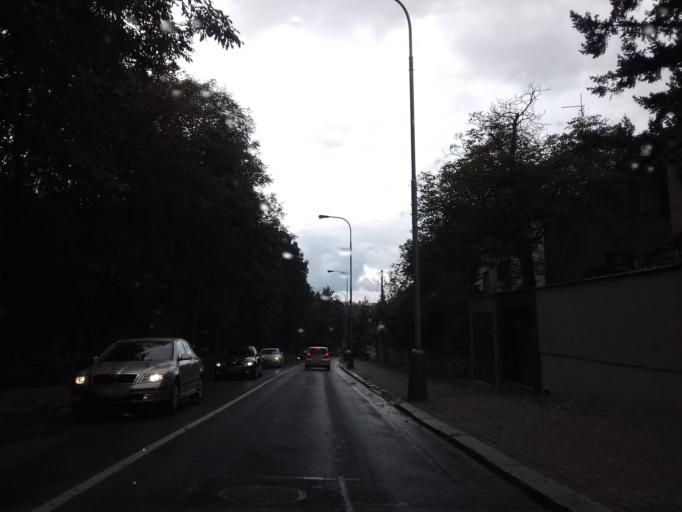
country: CZ
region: Praha
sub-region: Praha 4
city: Hodkovicky
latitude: 50.0256
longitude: 14.4202
